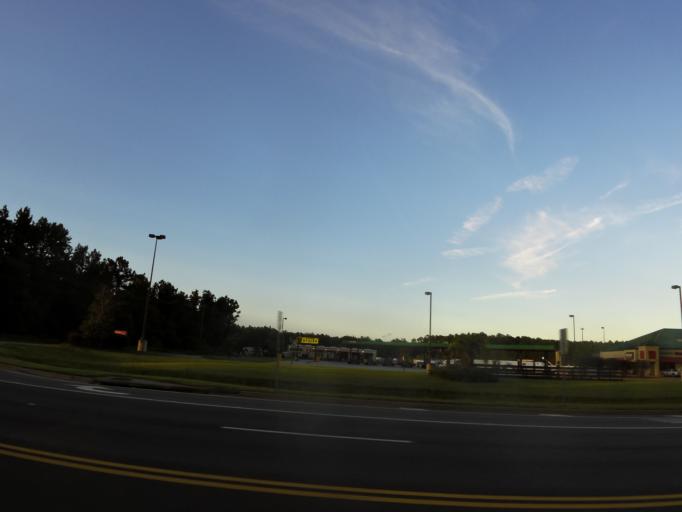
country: US
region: Georgia
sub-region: Camden County
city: Kingsland
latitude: 30.7937
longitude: -81.6677
